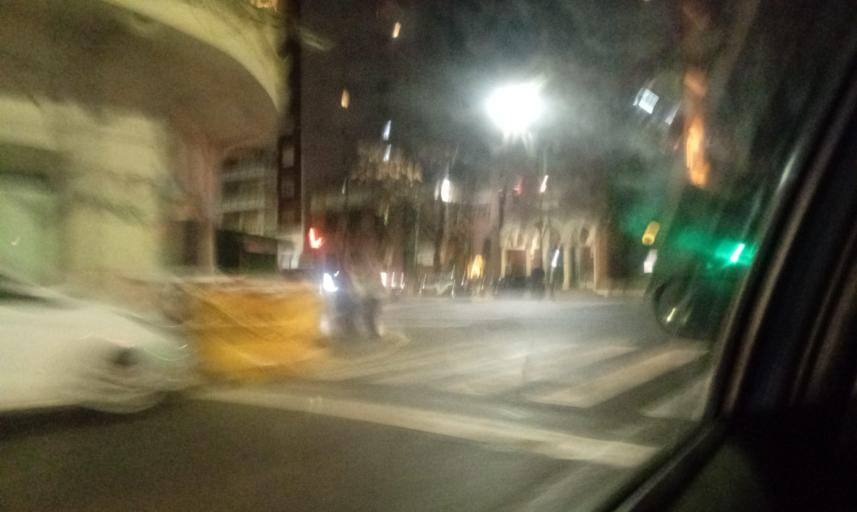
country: AR
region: Buenos Aires F.D.
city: Colegiales
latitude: -34.6183
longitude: -58.4289
